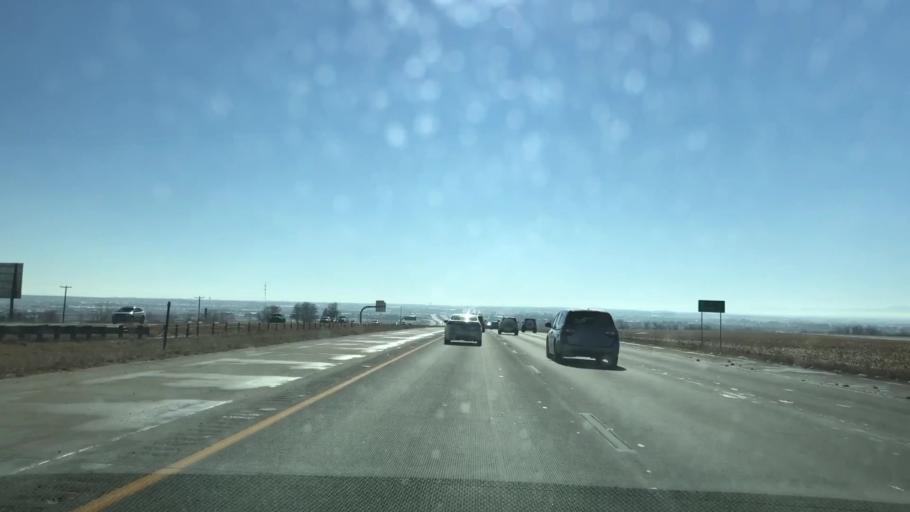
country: US
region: Colorado
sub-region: Weld County
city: Mead
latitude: 40.1886
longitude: -104.9805
